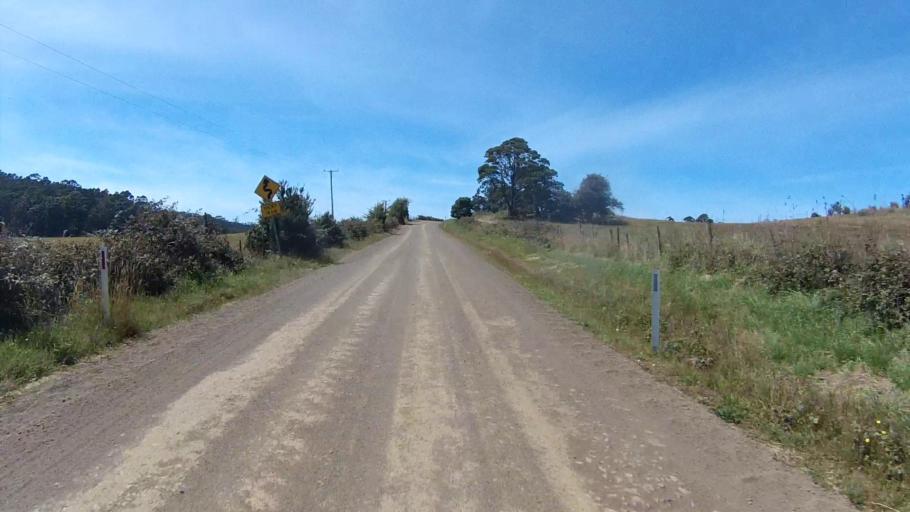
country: AU
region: Tasmania
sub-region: Sorell
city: Sorell
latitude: -42.7072
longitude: 147.7465
